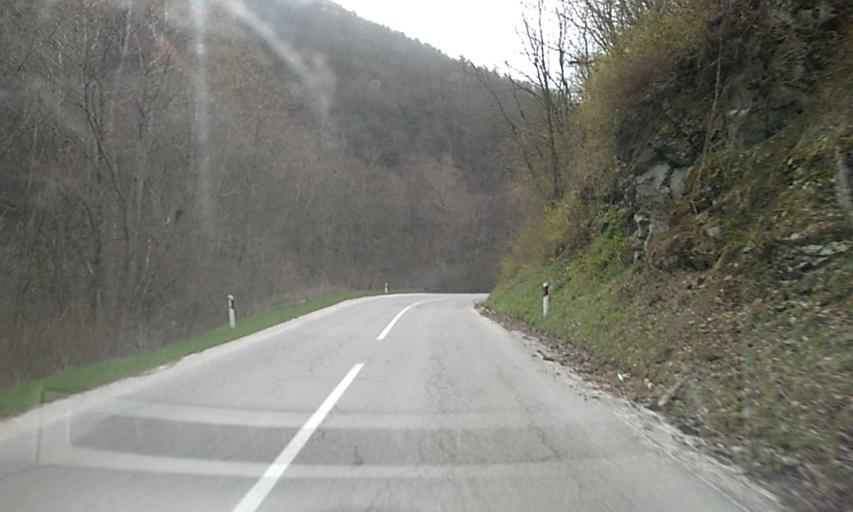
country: RS
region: Central Serbia
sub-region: Pcinjski Okrug
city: Bosilegrad
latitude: 42.5120
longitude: 22.4519
